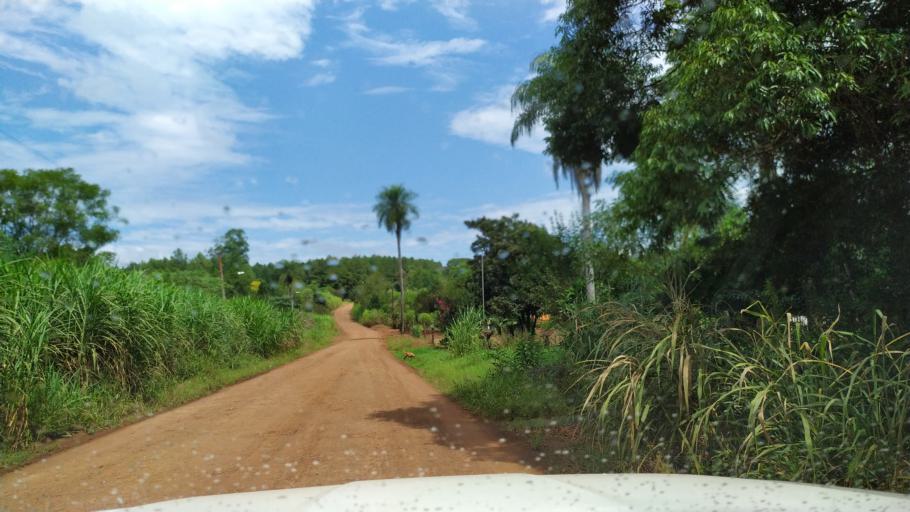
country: AR
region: Misiones
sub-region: Departamento de Eldorado
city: Eldorado
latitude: -26.4917
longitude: -54.5863
